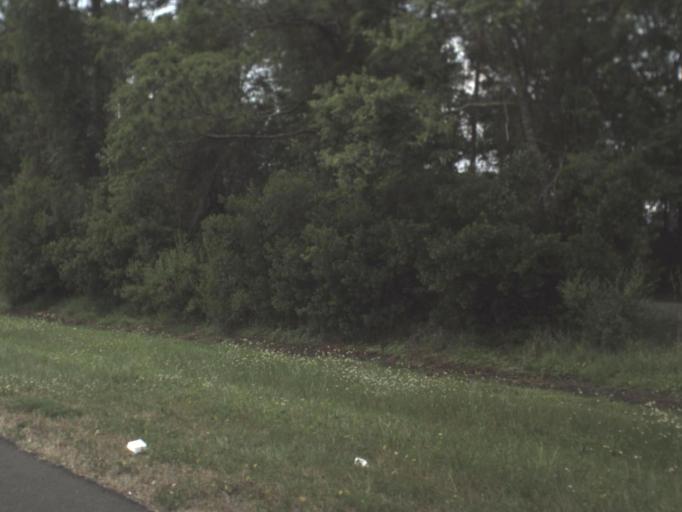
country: US
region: Florida
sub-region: Saint Johns County
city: Fruit Cove
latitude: 30.1006
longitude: -81.7059
